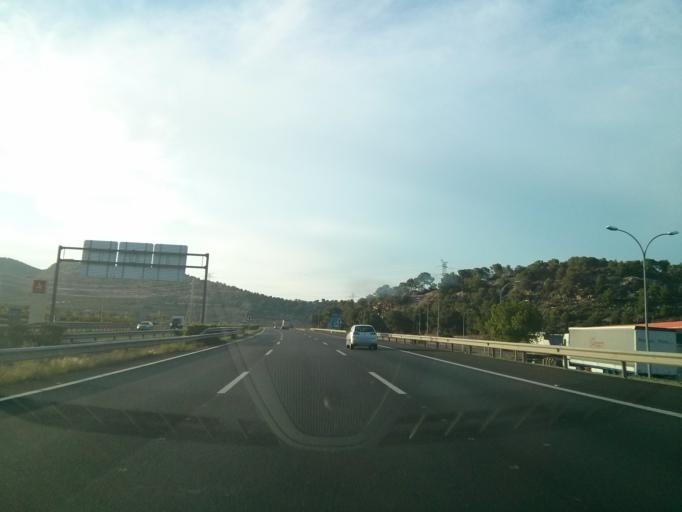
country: ES
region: Valencia
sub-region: Provincia de Valencia
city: Petres
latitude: 39.6502
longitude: -0.3015
